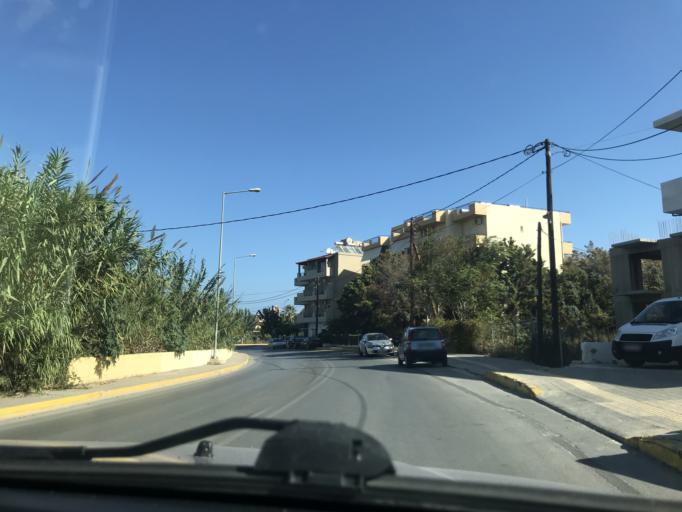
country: GR
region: Crete
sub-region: Nomos Irakleiou
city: Gazi
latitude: 35.3341
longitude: 25.0650
